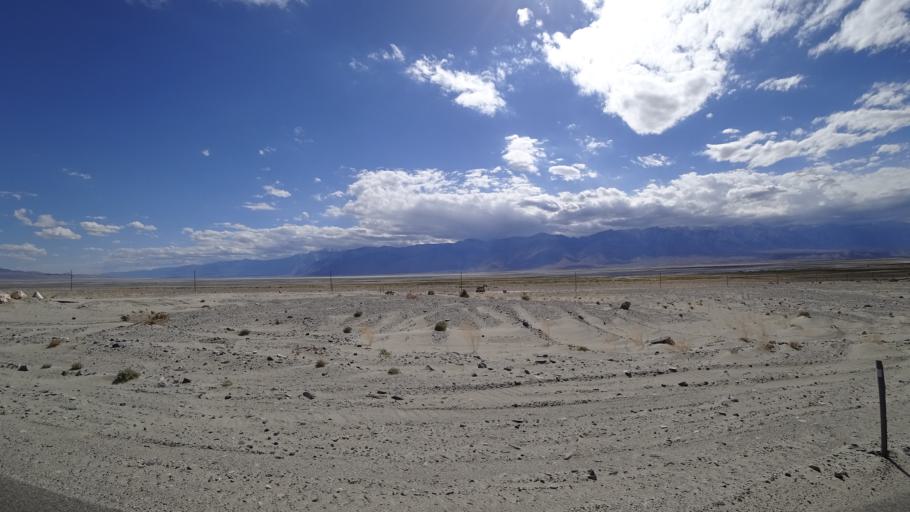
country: US
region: California
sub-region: Inyo County
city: Lone Pine
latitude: 36.5157
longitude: -117.8978
